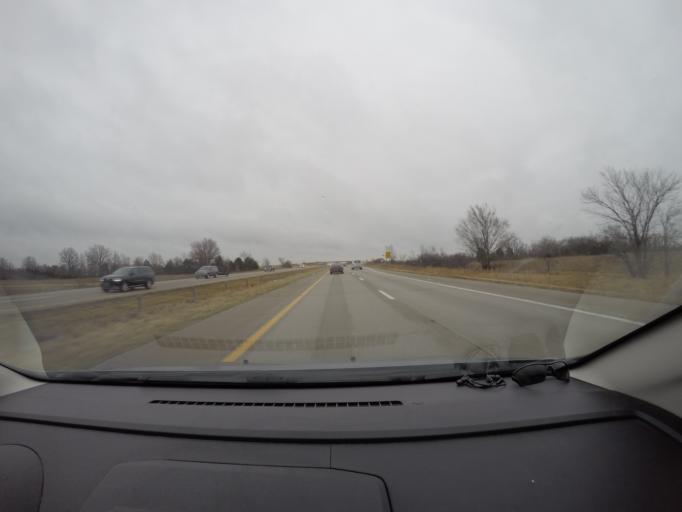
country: US
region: Missouri
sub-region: Montgomery County
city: Wellsville
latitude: 38.9113
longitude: -91.7073
